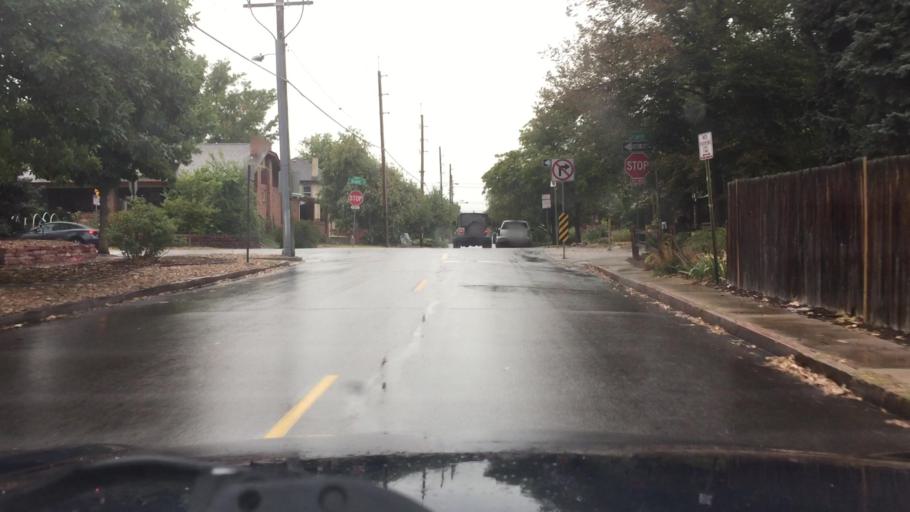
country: US
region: Colorado
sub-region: Denver County
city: Denver
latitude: 39.7210
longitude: -104.9834
